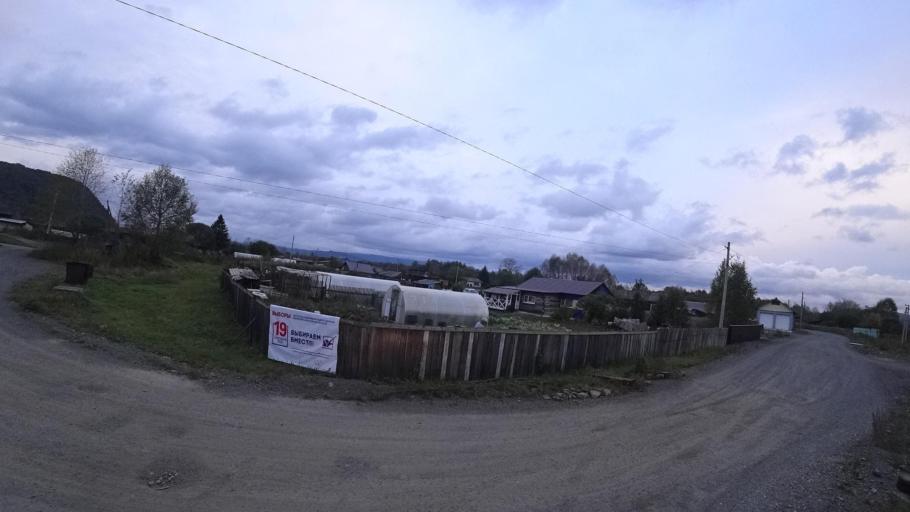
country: RU
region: Jewish Autonomous Oblast
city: Izvestkovyy
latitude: 48.9878
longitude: 131.5523
